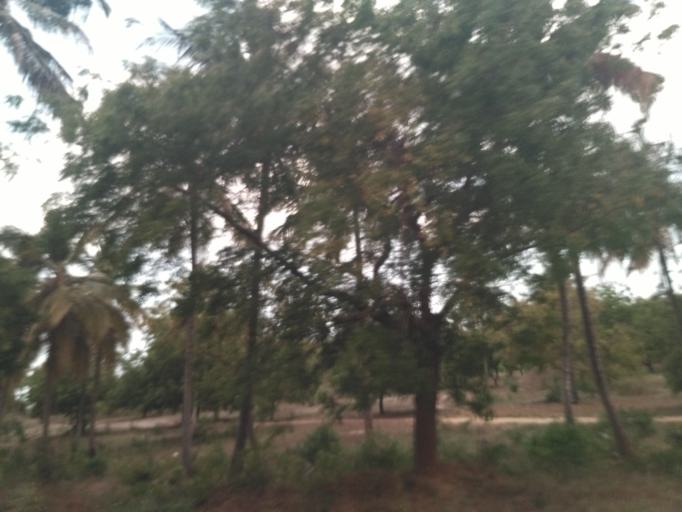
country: TZ
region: Dar es Salaam
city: Dar es Salaam
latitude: -6.8508
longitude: 39.3567
